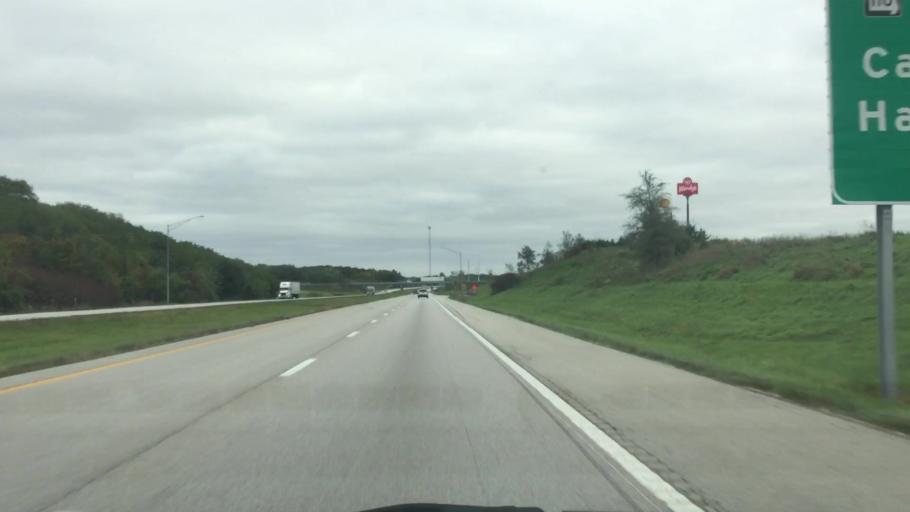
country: US
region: Missouri
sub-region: Clinton County
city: Cameron
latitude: 39.7483
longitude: -94.2199
